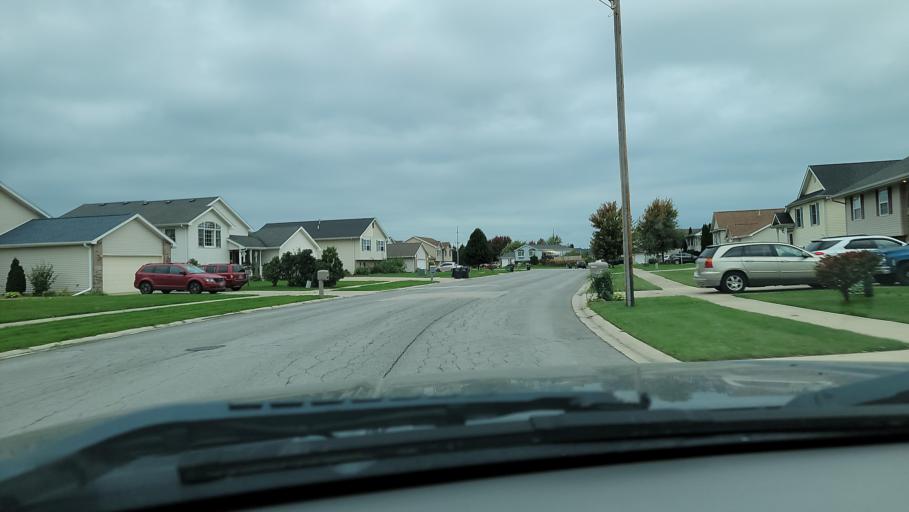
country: US
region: Indiana
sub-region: Porter County
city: Portage
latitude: 41.5616
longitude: -87.1615
